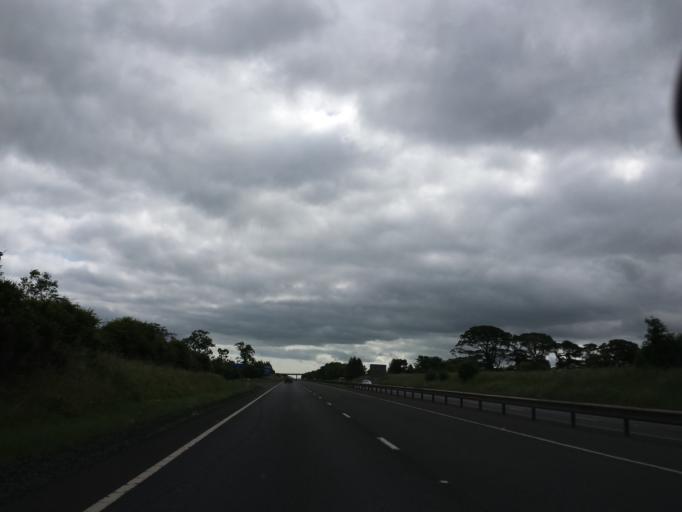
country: GB
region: Scotland
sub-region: East Lothian
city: Longniddry
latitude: 55.9522
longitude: -2.8645
